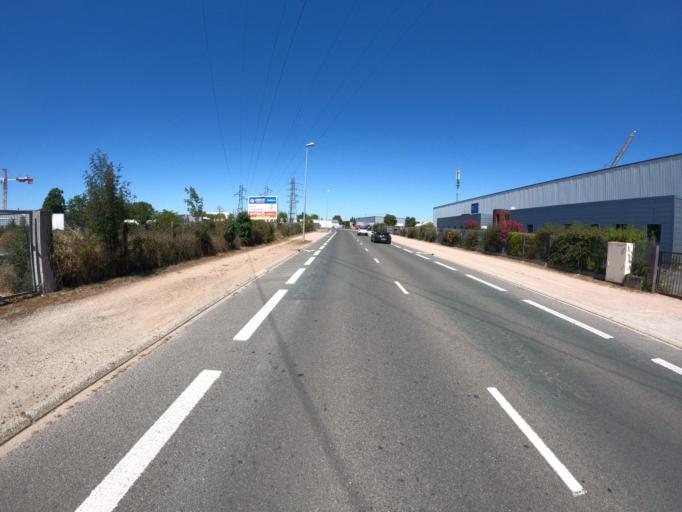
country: FR
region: Pays de la Loire
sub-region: Departement de la Vendee
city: Challans
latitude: 46.8477
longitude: -1.8592
